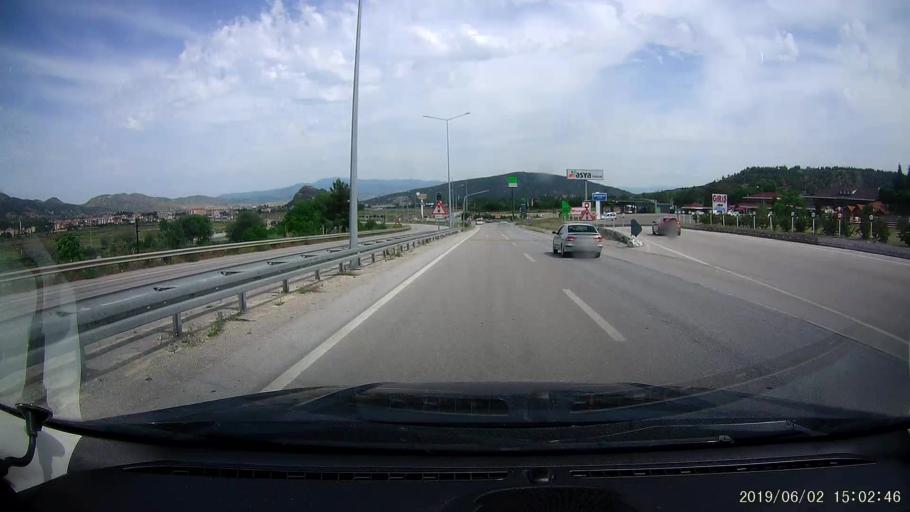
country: TR
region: Corum
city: Osmancik
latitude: 40.9785
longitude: 34.7715
